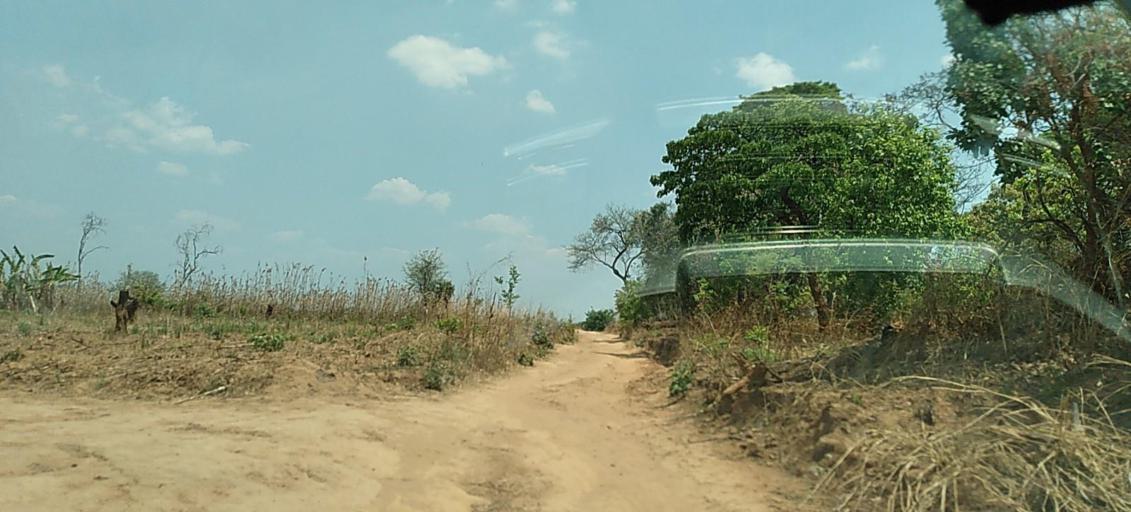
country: ZM
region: North-Western
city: Kasempa
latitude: -13.5306
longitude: 25.8228
